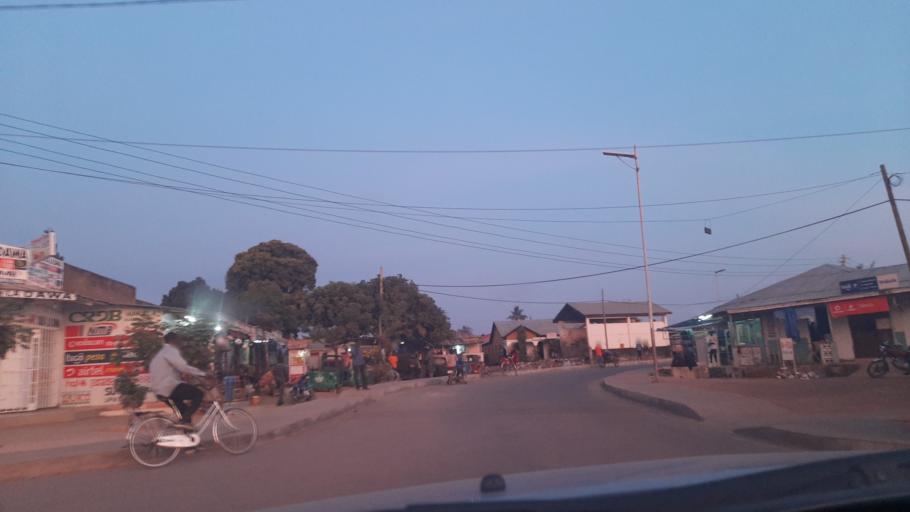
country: TZ
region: Singida
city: Singida
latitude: -4.8208
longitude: 34.7513
